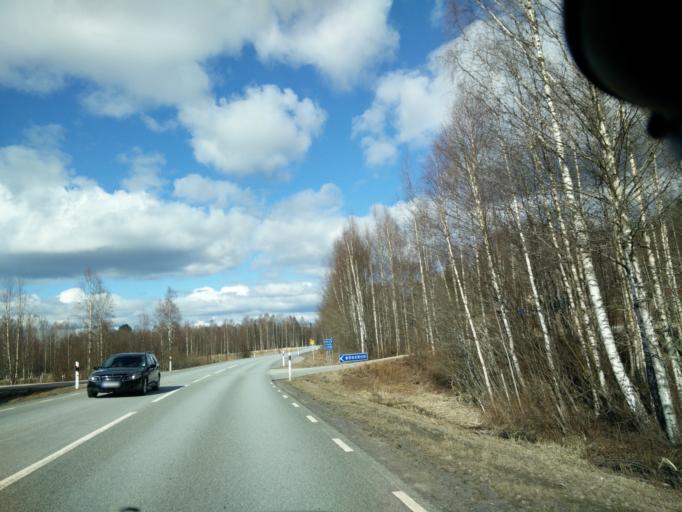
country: SE
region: Vaermland
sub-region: Munkfors Kommun
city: Munkfors
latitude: 59.8605
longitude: 13.5612
